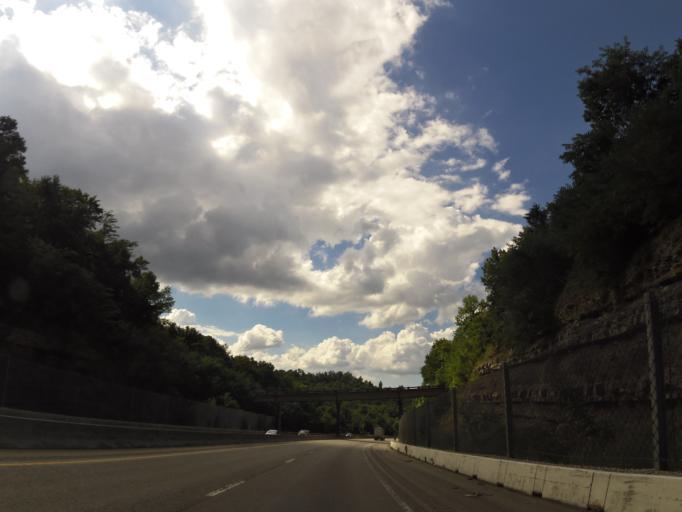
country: US
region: Tennessee
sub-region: Putnam County
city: Monterey
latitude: 36.1305
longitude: -85.3564
